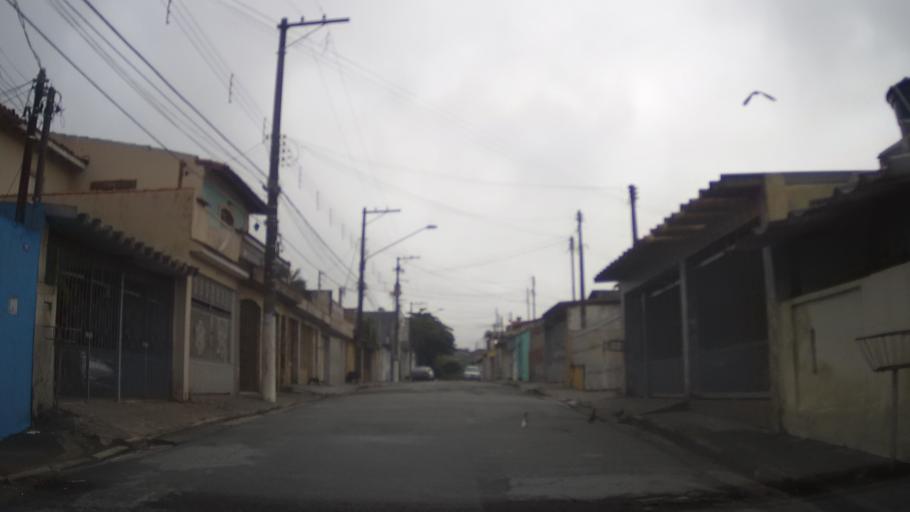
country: BR
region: Sao Paulo
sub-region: Guarulhos
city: Guarulhos
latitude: -23.4993
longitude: -46.5577
